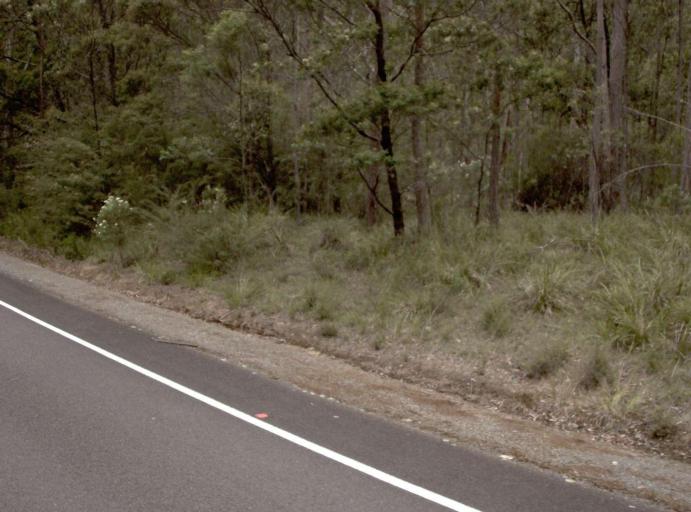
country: AU
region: New South Wales
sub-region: Bombala
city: Bombala
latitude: -37.2752
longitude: 149.2255
